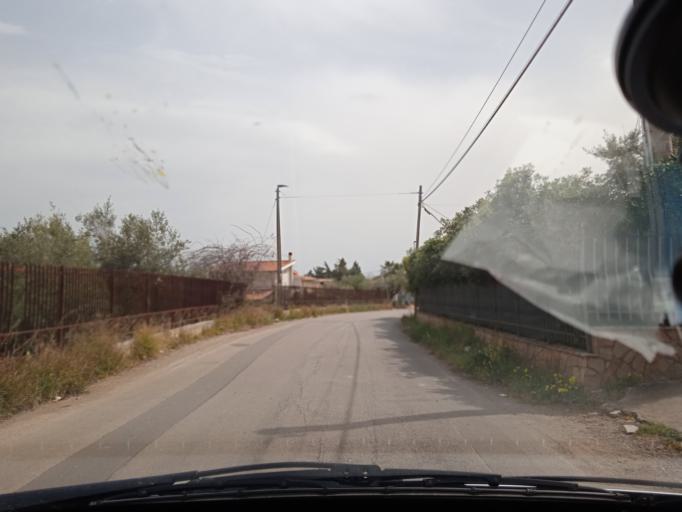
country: IT
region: Sicily
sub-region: Palermo
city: Torre Colonna-Sperone
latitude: 38.0291
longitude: 13.5707
